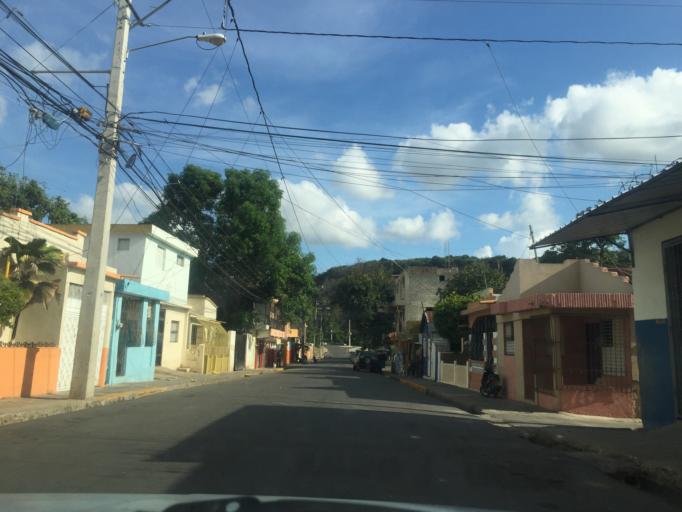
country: DO
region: Santiago
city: Santiago de los Caballeros
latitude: 19.4515
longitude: -70.7130
